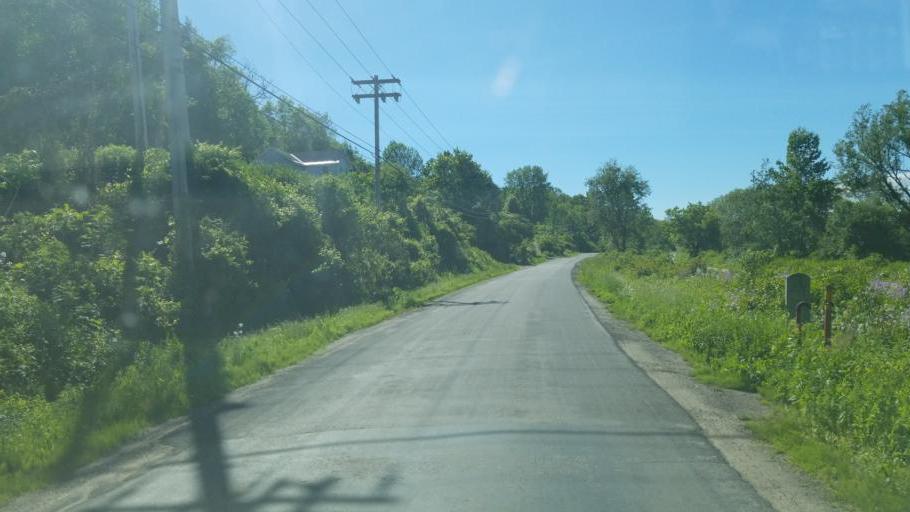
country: US
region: New York
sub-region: Montgomery County
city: Canajoharie
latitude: 42.9051
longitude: -74.5868
